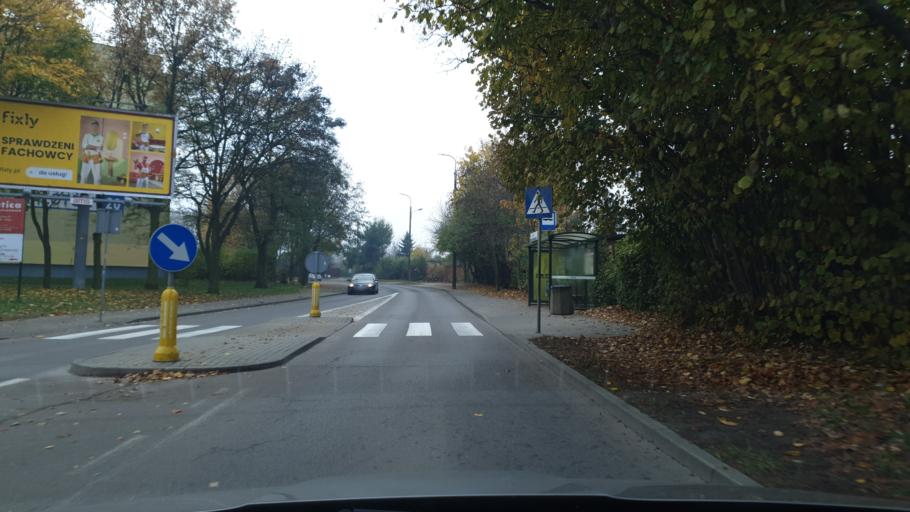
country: PL
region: Pomeranian Voivodeship
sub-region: Sopot
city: Sopot
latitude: 54.3969
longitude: 18.5884
